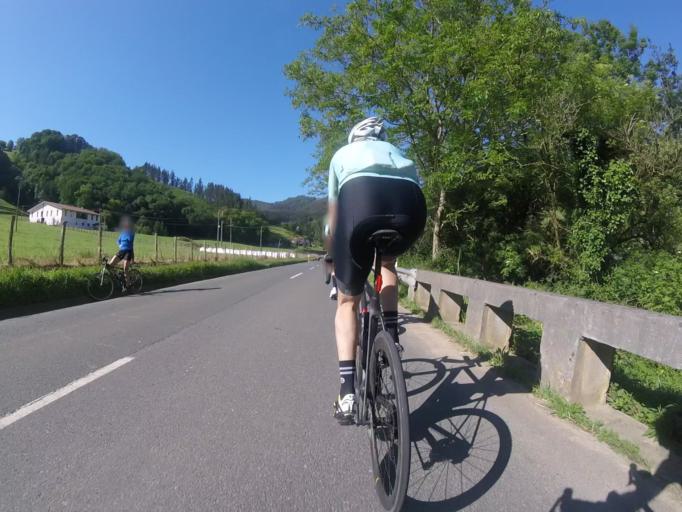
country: ES
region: Basque Country
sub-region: Provincia de Guipuzcoa
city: Beizama
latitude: 43.1447
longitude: -2.2332
